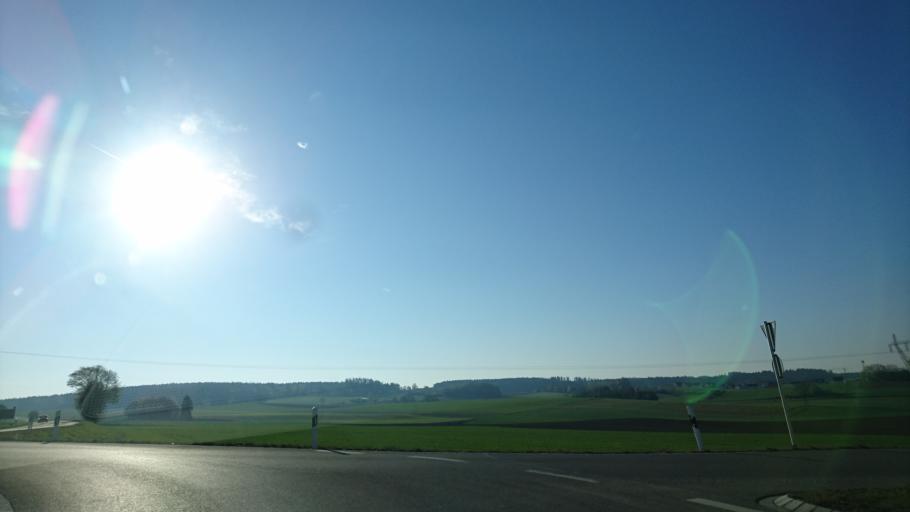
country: DE
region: Bavaria
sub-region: Swabia
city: Bonstetten
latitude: 48.4366
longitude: 10.7170
